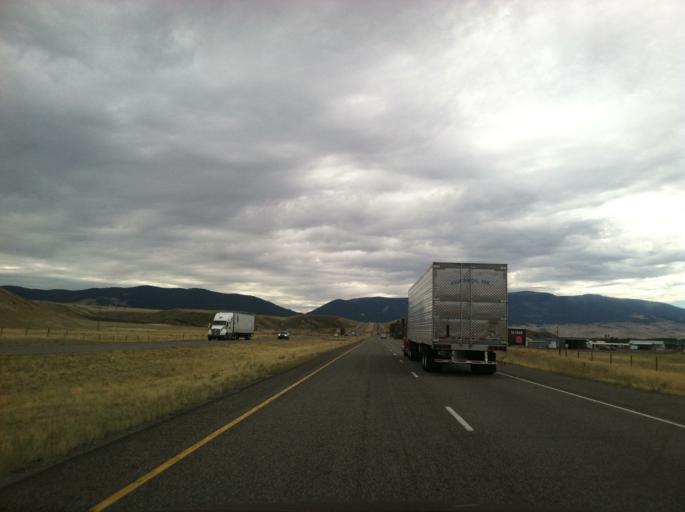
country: US
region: Montana
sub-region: Park County
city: Livingston
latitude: 45.6833
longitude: -110.5070
